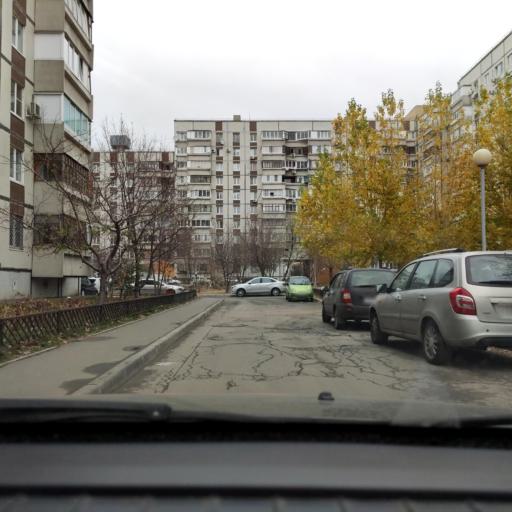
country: RU
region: Samara
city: Tol'yatti
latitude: 53.5449
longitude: 49.3634
